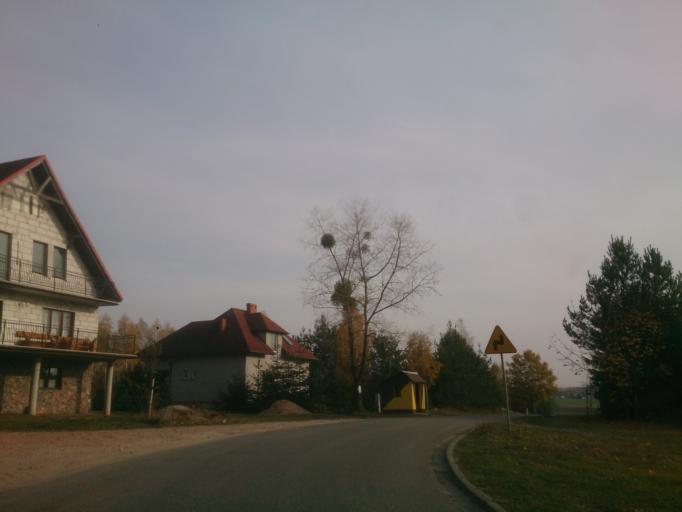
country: PL
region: Kujawsko-Pomorskie
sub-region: Powiat brodnicki
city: Brodnica
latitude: 53.3386
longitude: 19.3540
